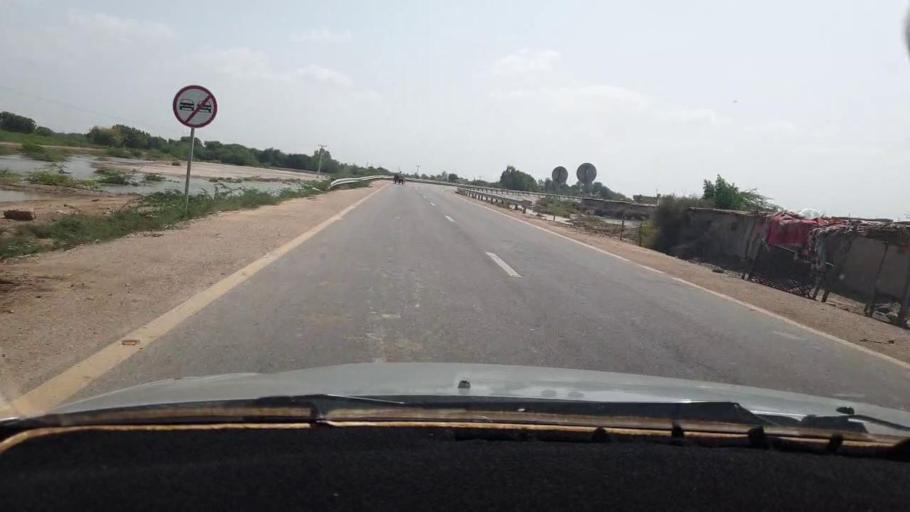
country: PK
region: Sindh
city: Digri
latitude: 25.1487
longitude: 69.1261
